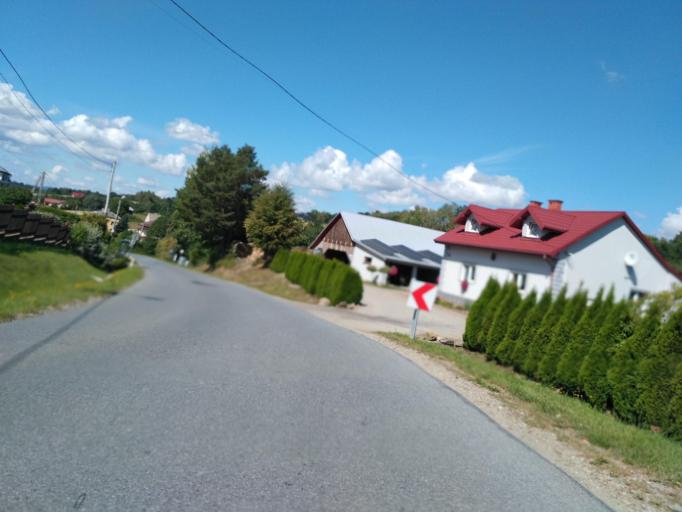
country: PL
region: Subcarpathian Voivodeship
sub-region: Powiat jasielski
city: Skolyszyn
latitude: 49.7908
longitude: 21.3412
